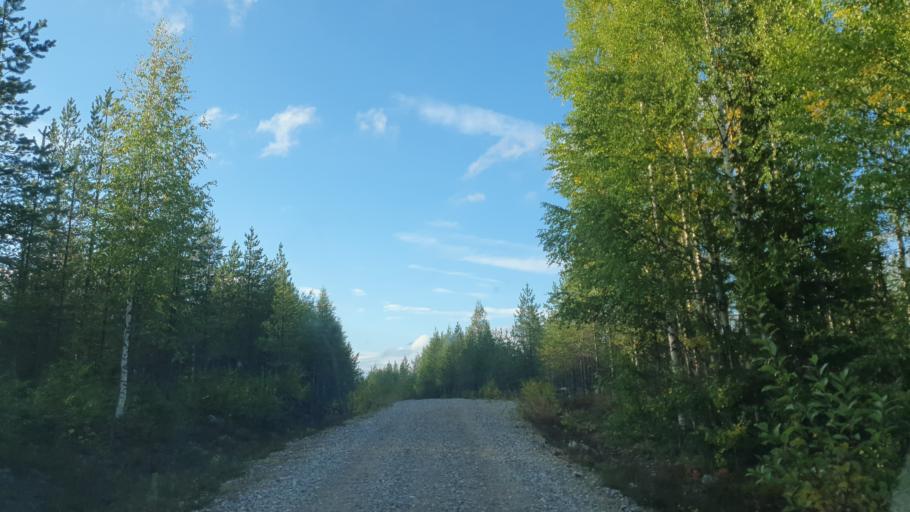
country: FI
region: Kainuu
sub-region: Kehys-Kainuu
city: Kuhmo
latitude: 64.3324
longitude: 30.0119
